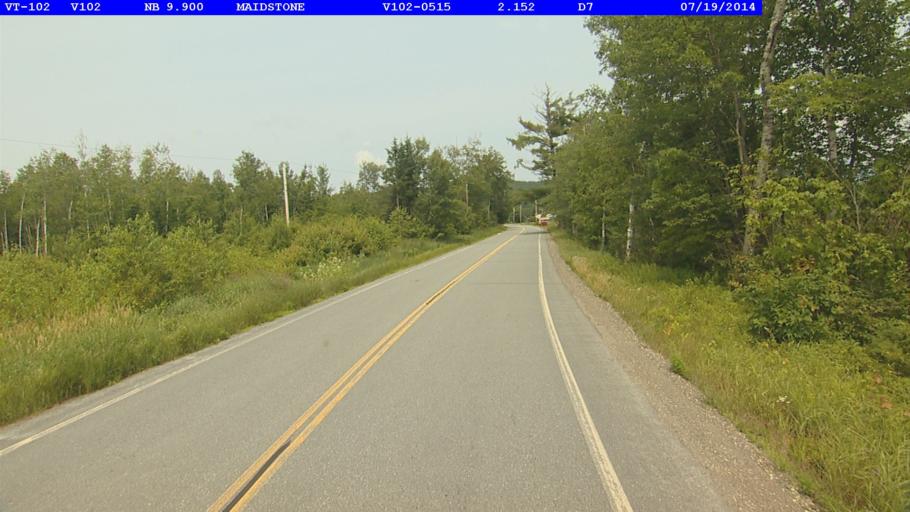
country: US
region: Vermont
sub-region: Essex County
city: Guildhall
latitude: 44.5948
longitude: -71.5591
